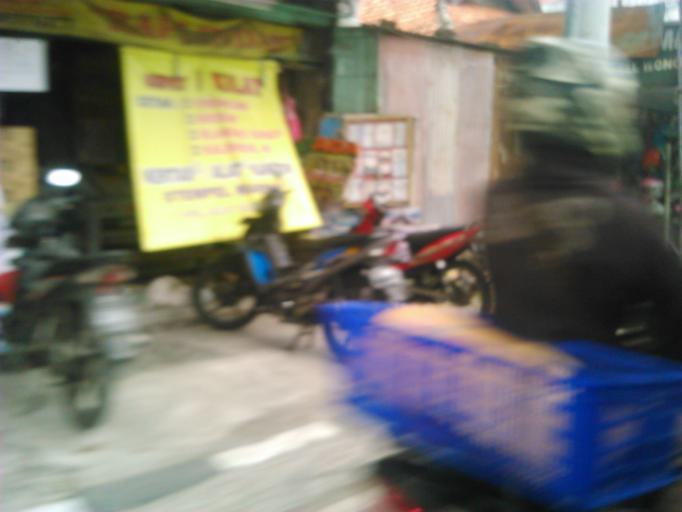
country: ID
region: East Java
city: Gubengairlangga
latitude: -7.2722
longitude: 112.7278
